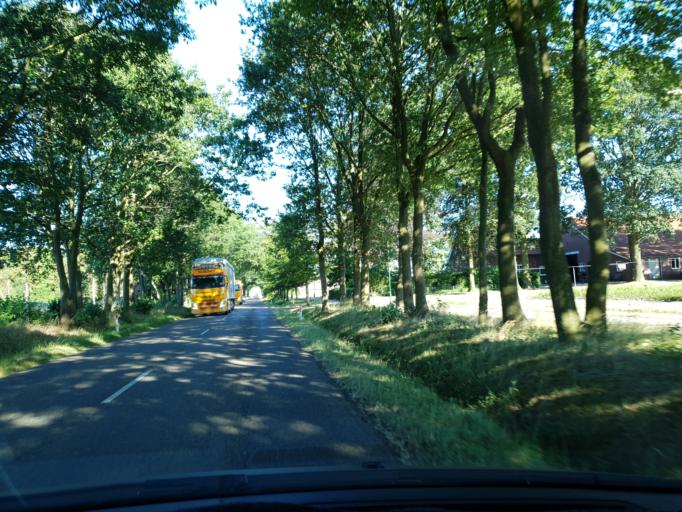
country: NL
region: North Brabant
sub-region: Gemeente Zundert
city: Zundert
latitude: 51.4761
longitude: 4.6439
